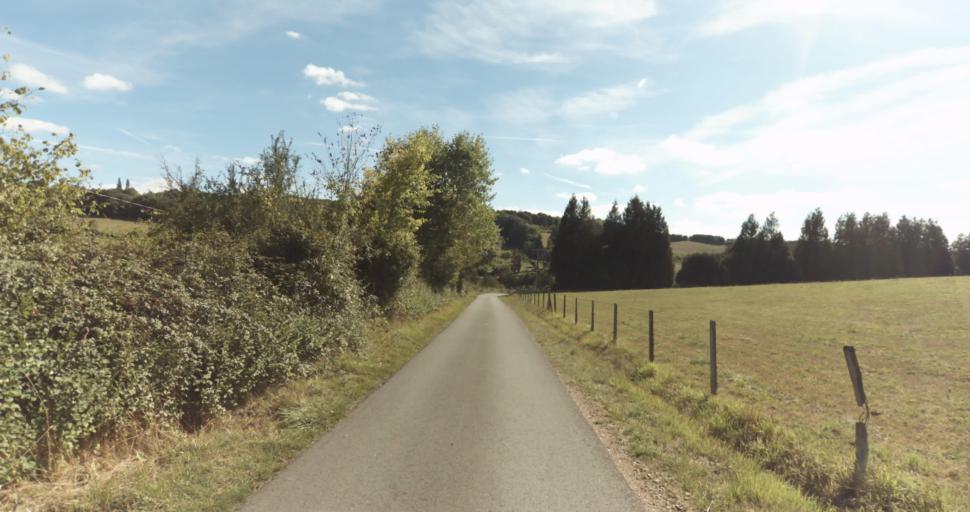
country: FR
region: Lower Normandy
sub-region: Departement de l'Orne
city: Vimoutiers
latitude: 48.9034
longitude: 0.1635
